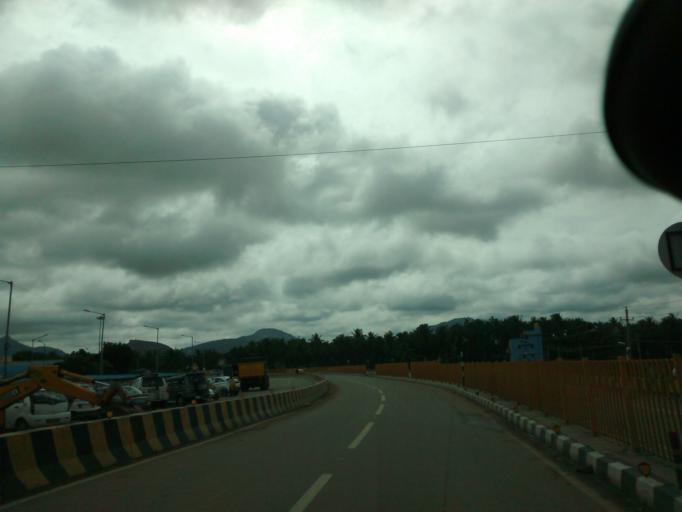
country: IN
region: Karnataka
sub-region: Tumkur
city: Tumkur
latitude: 13.3693
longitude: 77.1073
